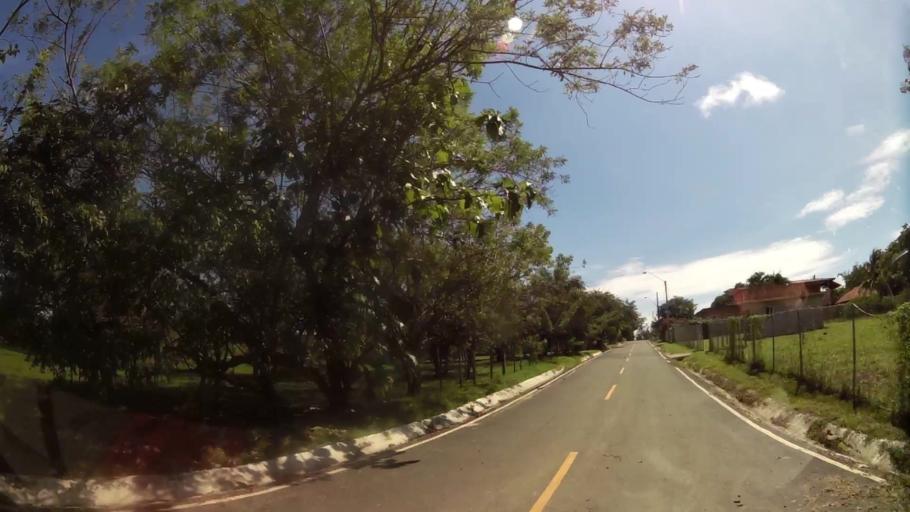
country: PA
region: Panama
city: Nueva Gorgona
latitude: 8.5628
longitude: -79.8750
